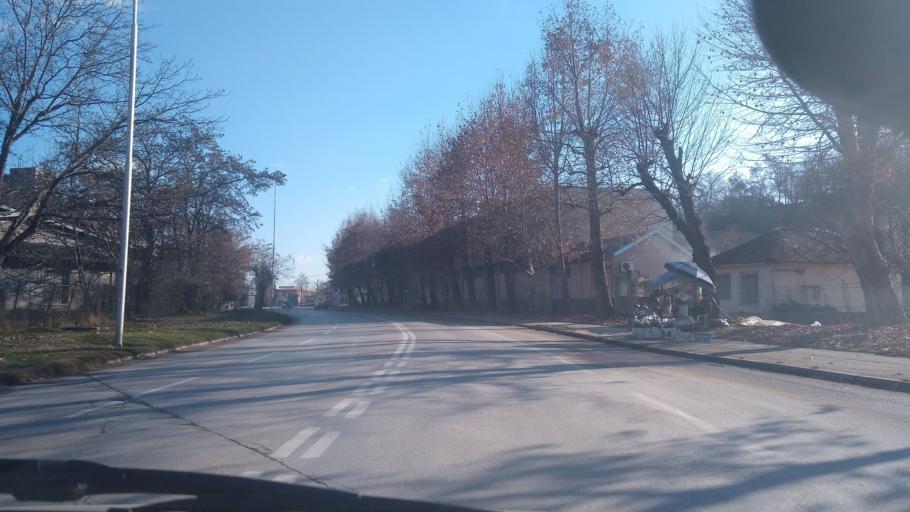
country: MK
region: Bitola
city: Bitola
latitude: 41.0170
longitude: 21.3426
